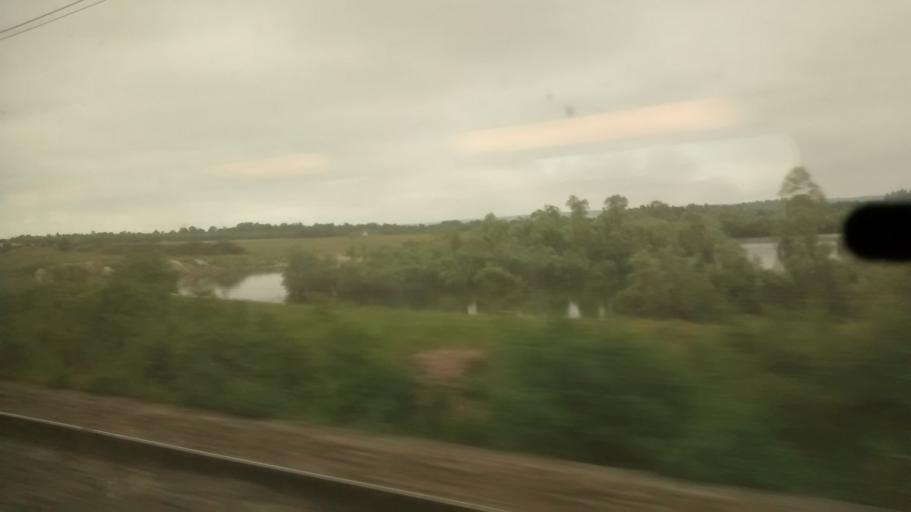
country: FR
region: Bourgogne
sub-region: Departement de l'Yonne
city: Villeneuve-la-Guyard
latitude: 48.3719
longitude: 3.0736
